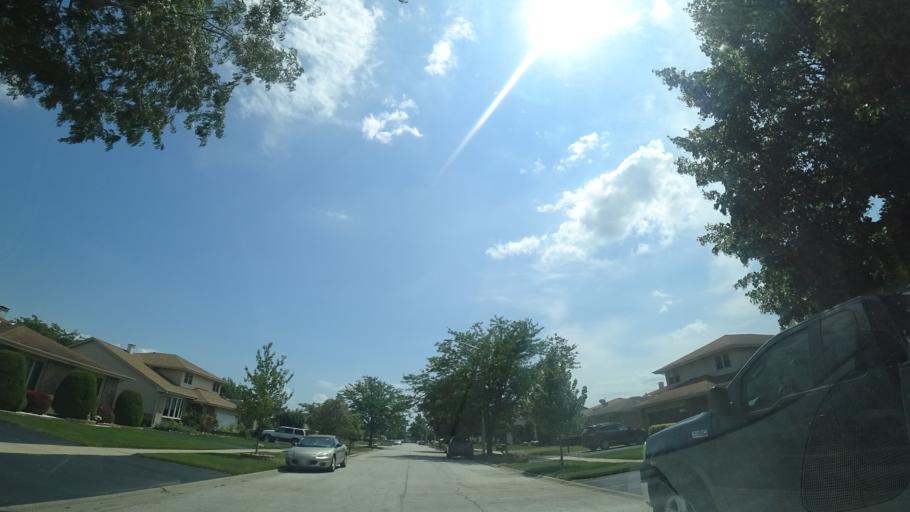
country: US
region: Illinois
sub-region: Cook County
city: Crestwood
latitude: 41.6741
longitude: -87.7519
